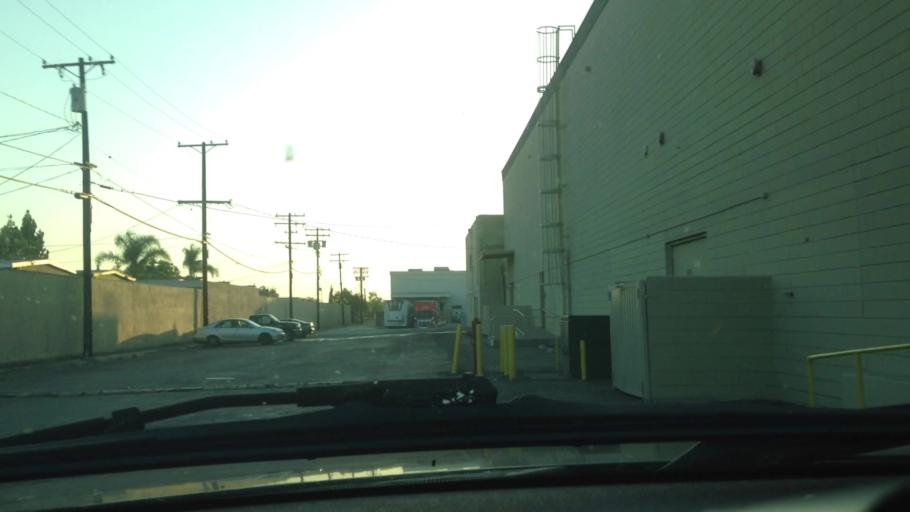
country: US
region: California
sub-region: Orange County
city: Anaheim
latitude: 33.8374
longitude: -117.8866
